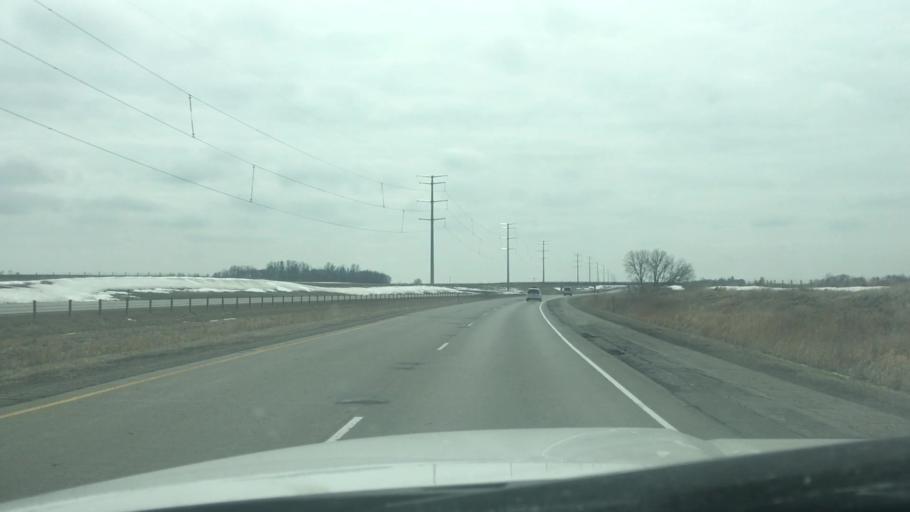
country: US
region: Minnesota
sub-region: Clay County
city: Barnesville
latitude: 46.5218
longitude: -96.2913
